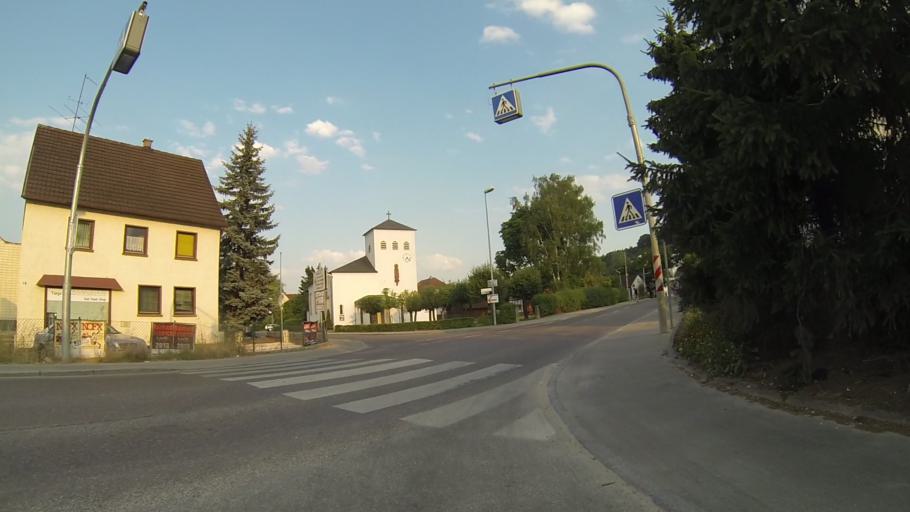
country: DE
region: Baden-Wuerttemberg
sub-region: Tuebingen Region
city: Dornstadt
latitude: 48.4201
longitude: 9.9073
